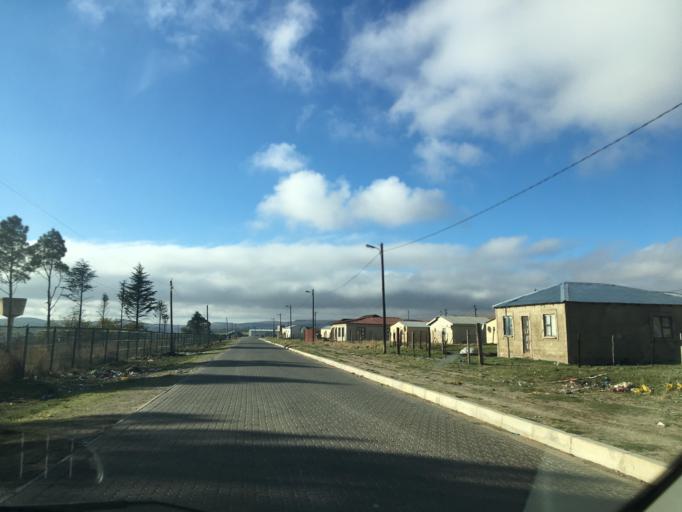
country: ZA
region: Eastern Cape
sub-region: Chris Hani District Municipality
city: Elliot
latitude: -31.3369
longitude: 27.8359
